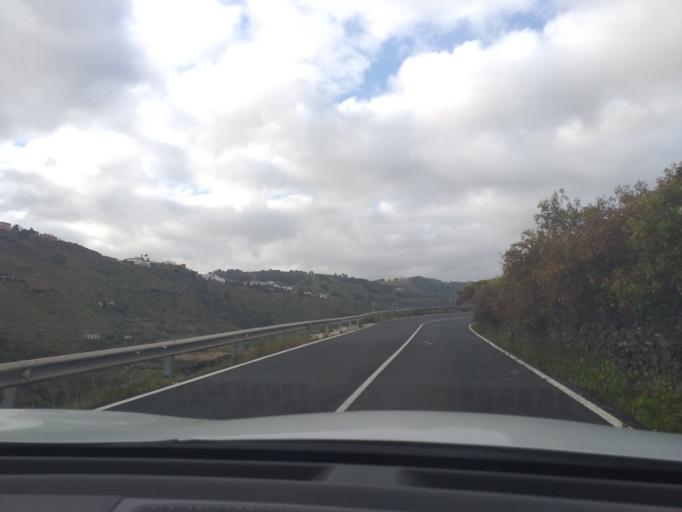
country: ES
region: Canary Islands
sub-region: Provincia de Las Palmas
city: Arucas
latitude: 28.1063
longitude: -15.5051
